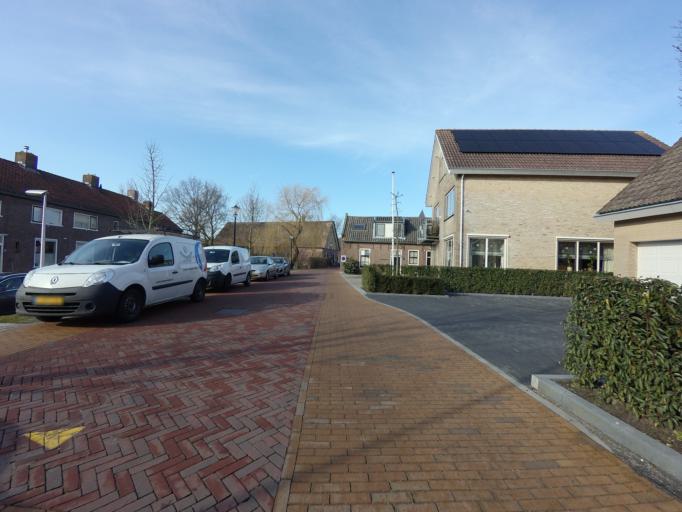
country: NL
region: South Holland
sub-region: Gemeente Hardinxveld-Giessendam
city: Neder-Hardinxveld
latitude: 51.8428
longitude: 4.8664
